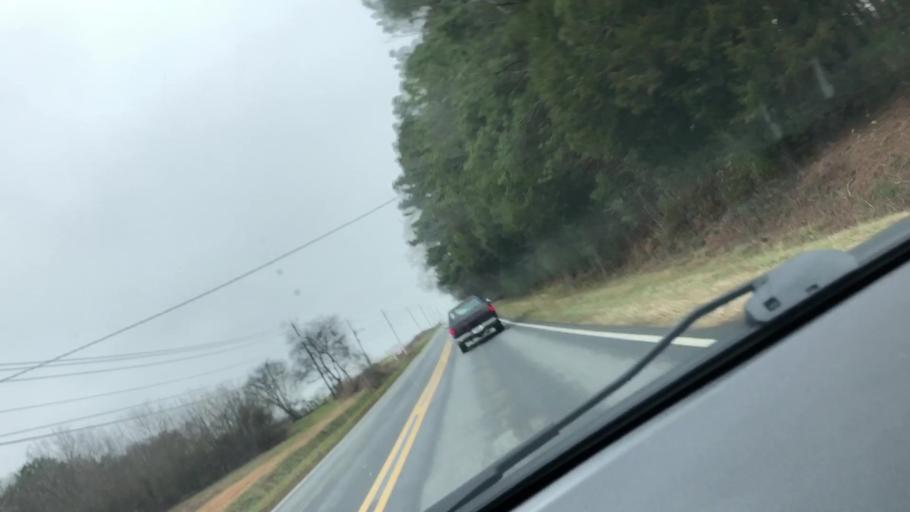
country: US
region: Georgia
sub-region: Bartow County
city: Cartersville
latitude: 34.1891
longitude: -84.8319
